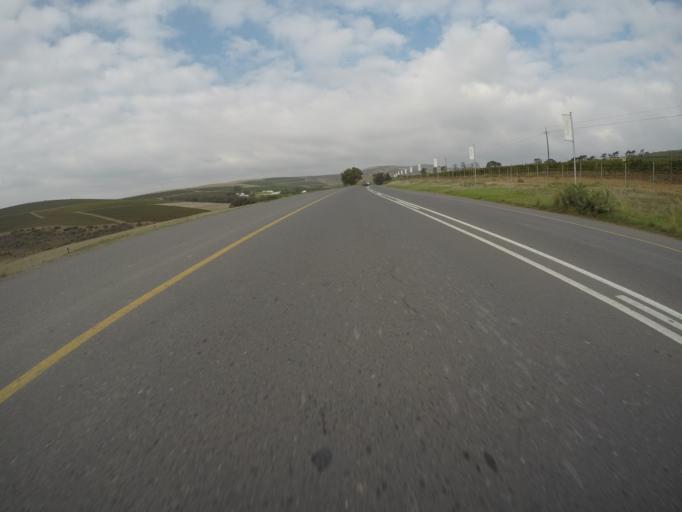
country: ZA
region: Western Cape
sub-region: City of Cape Town
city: Sunset Beach
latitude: -33.8206
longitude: 18.5635
